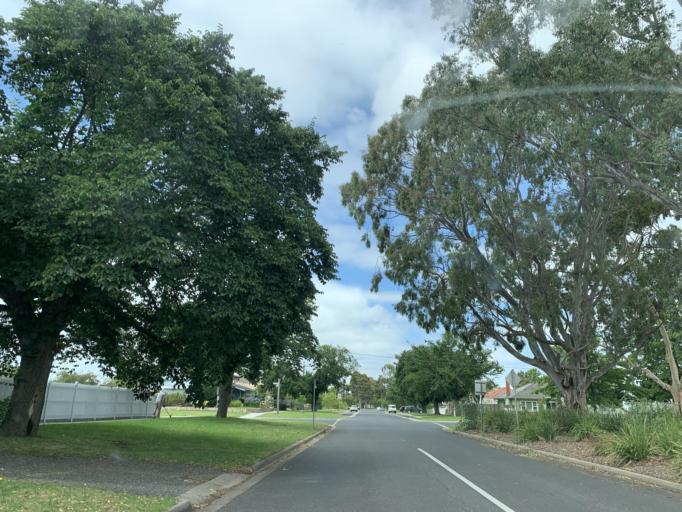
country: AU
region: Victoria
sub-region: Wellington
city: Sale
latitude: -38.1071
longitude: 147.0732
